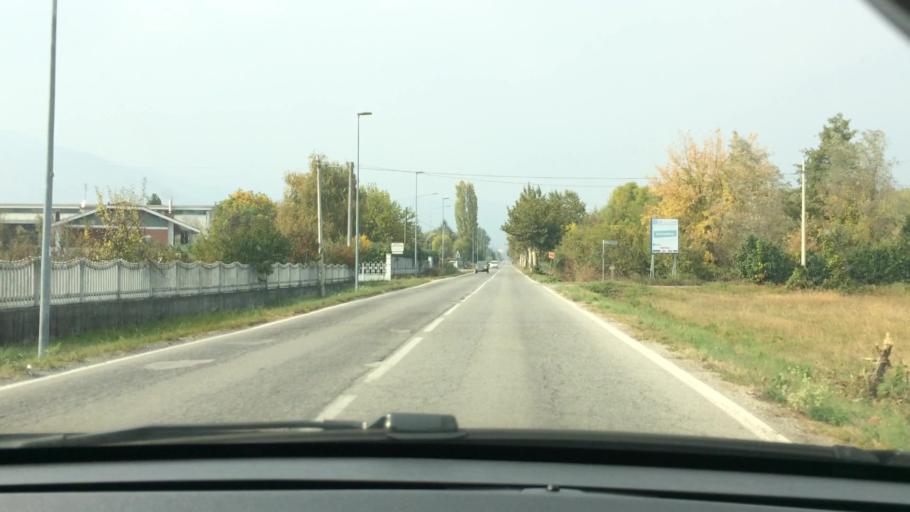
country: IT
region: Piedmont
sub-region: Provincia di Torino
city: Cumiana
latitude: 44.9607
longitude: 7.4024
